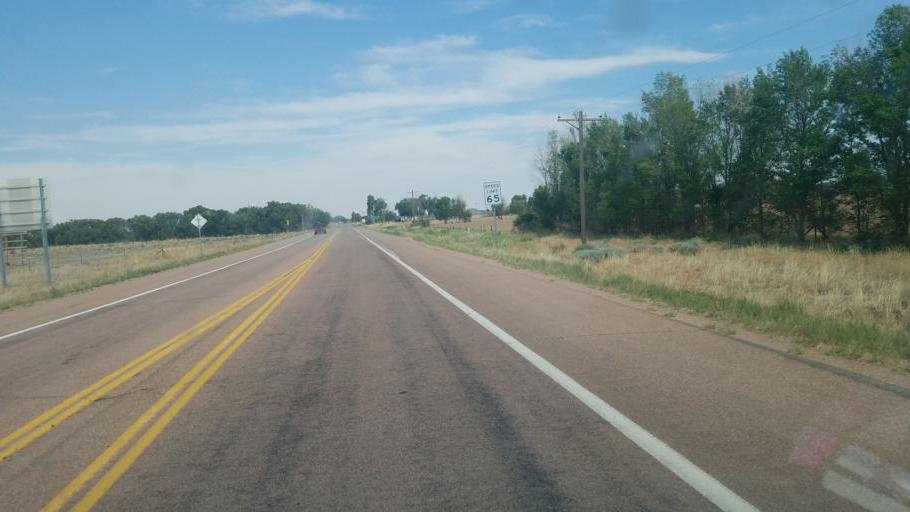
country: US
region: Colorado
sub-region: Pueblo County
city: Pueblo
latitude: 38.2332
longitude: -104.3228
